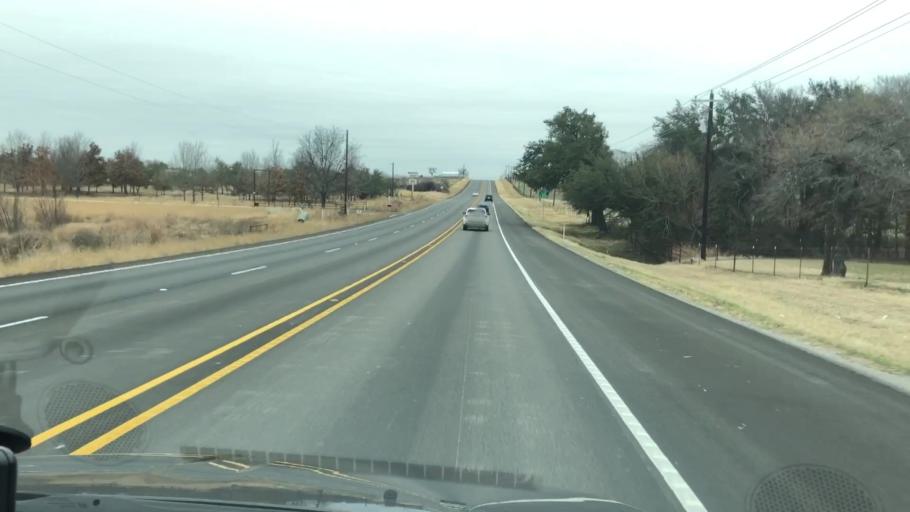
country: US
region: Texas
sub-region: Erath County
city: Stephenville
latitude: 32.2892
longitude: -98.1912
